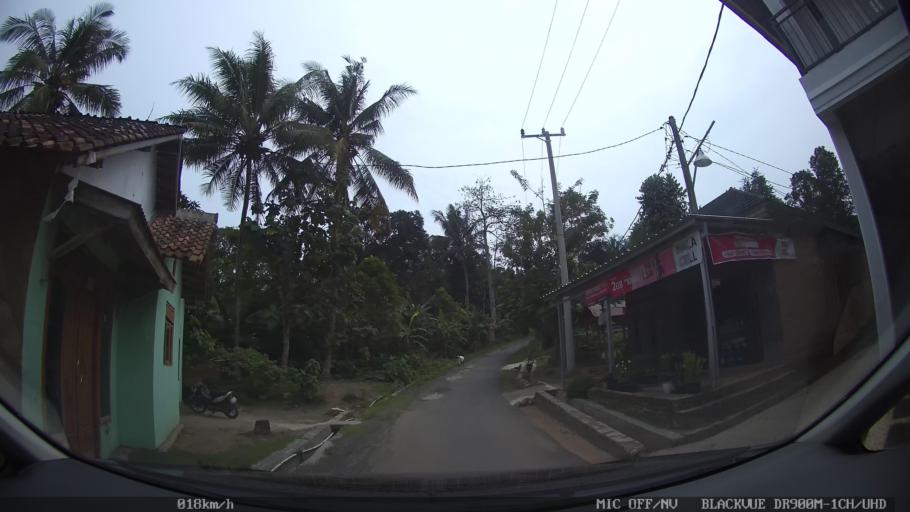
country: ID
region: Lampung
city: Bandarlampung
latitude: -5.4237
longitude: 105.3043
